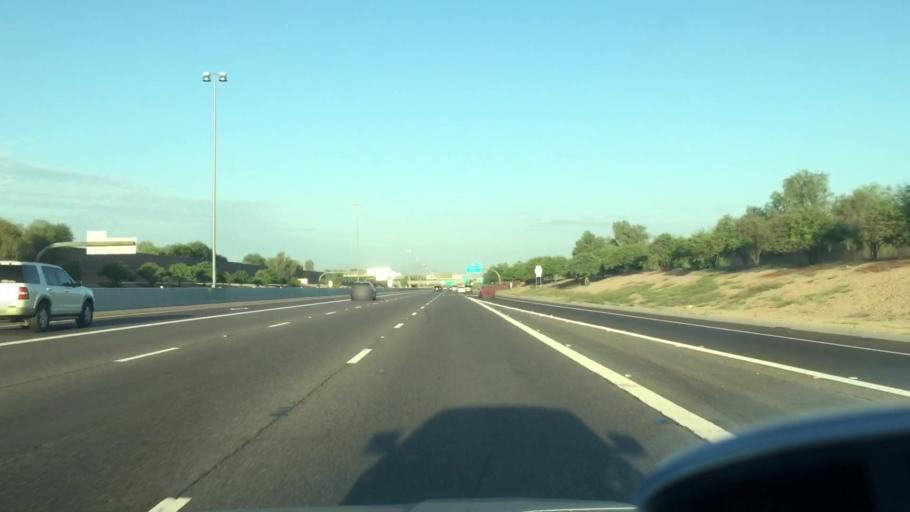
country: US
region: Arizona
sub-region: Maricopa County
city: Chandler
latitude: 33.2874
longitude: -111.8632
